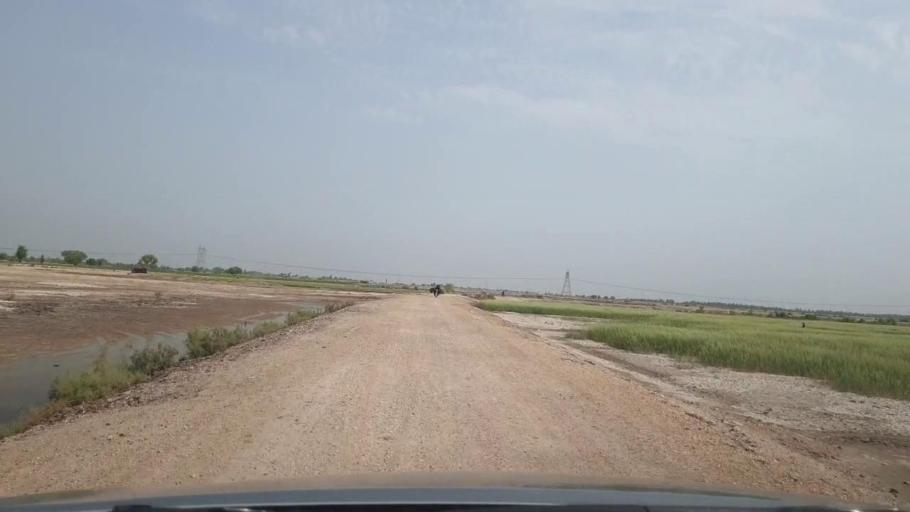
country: PK
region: Sindh
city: Rohri
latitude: 27.6673
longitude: 69.0258
